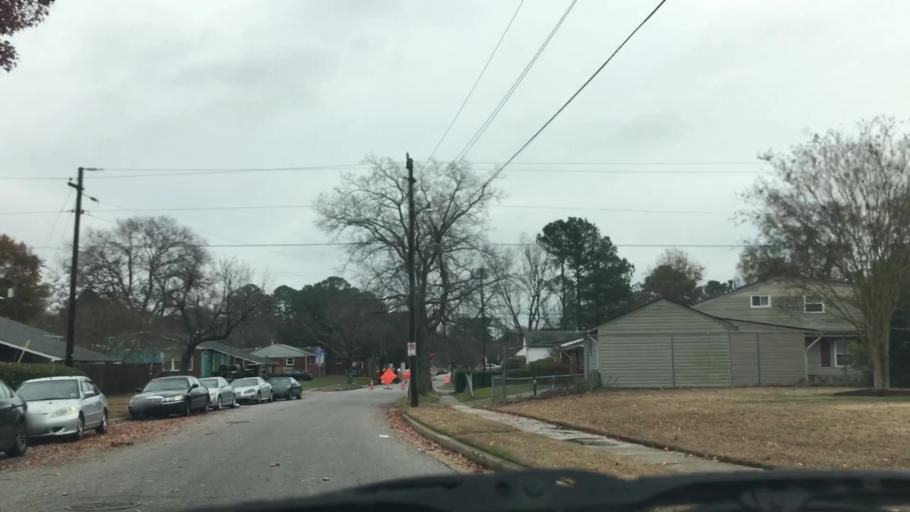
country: US
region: Virginia
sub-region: City of Norfolk
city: Norfolk
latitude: 36.8757
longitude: -76.2368
